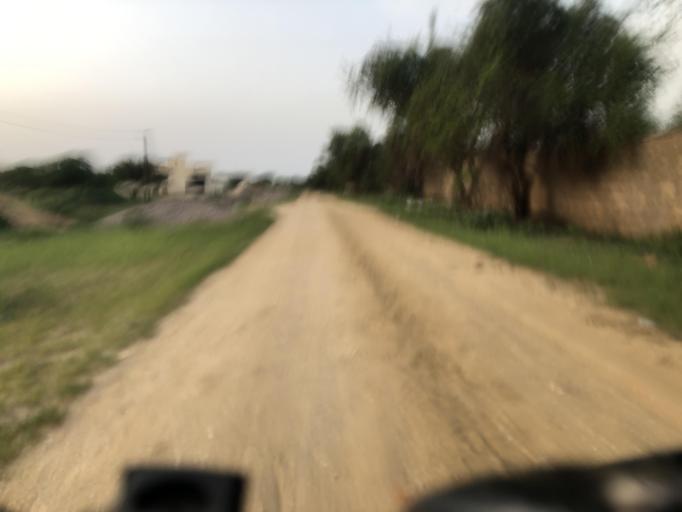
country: SN
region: Saint-Louis
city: Saint-Louis
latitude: 16.0552
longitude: -16.4316
